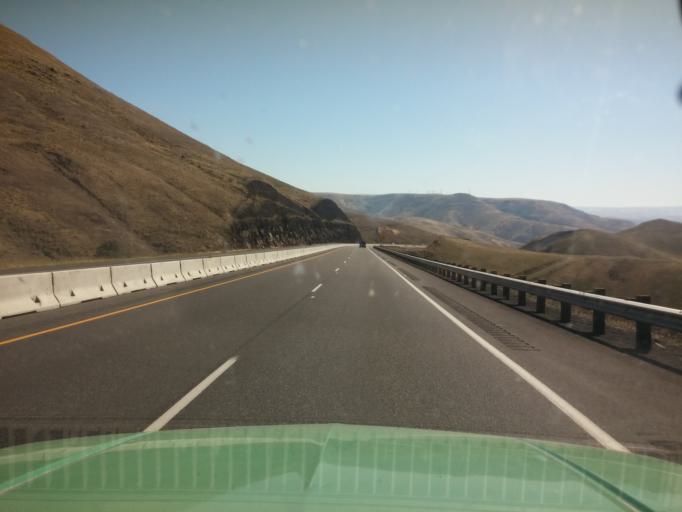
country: US
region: Idaho
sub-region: Nez Perce County
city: Lewiston
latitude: 46.4607
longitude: -116.9736
